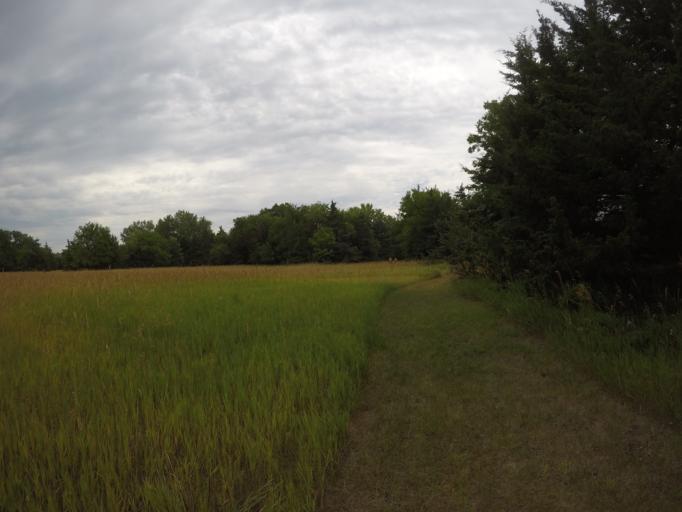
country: US
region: Nebraska
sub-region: Buffalo County
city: Kearney
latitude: 40.6572
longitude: -99.0111
